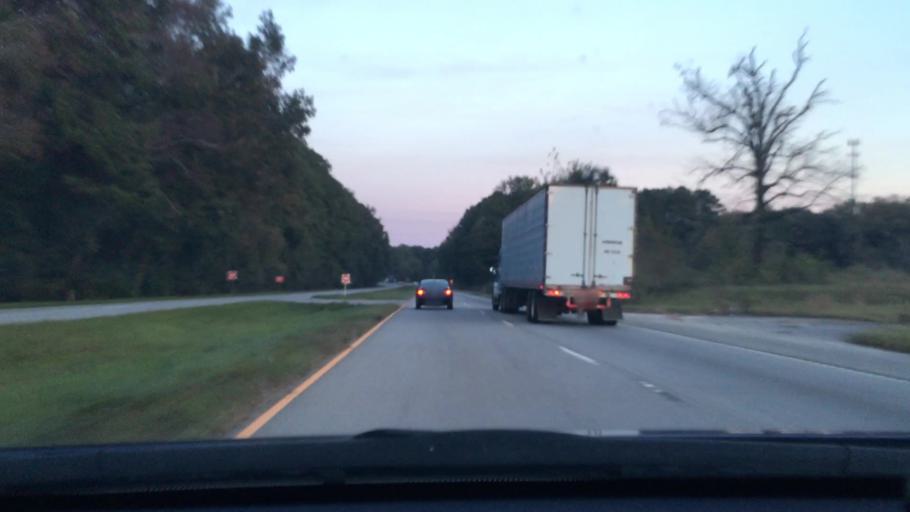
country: US
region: South Carolina
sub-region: Sumter County
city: Stateburg
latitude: 33.9434
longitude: -80.6548
